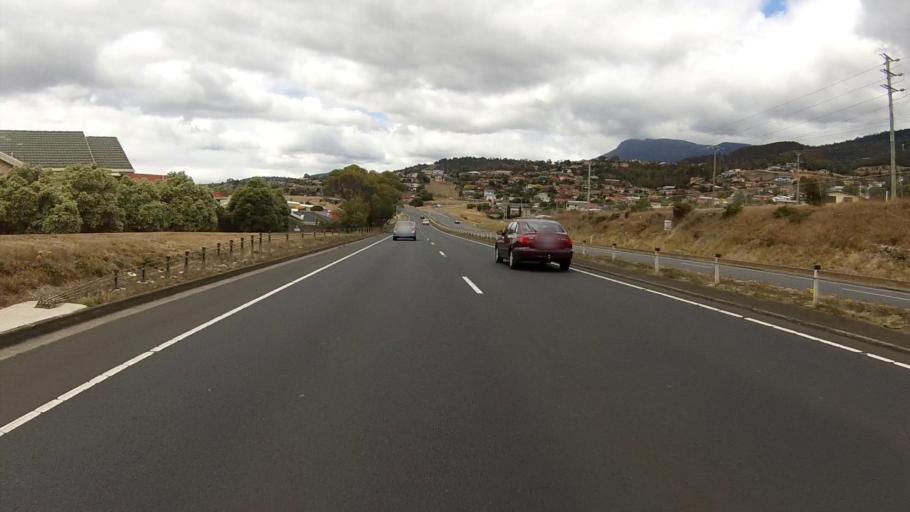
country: AU
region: Tasmania
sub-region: Glenorchy
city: Berriedale
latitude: -42.8115
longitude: 147.2504
